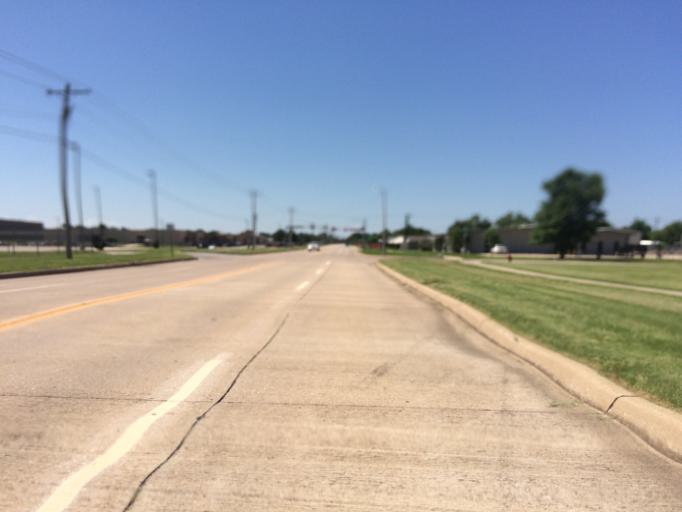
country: US
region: Oklahoma
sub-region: Cleveland County
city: Norman
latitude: 35.2434
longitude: -97.4501
